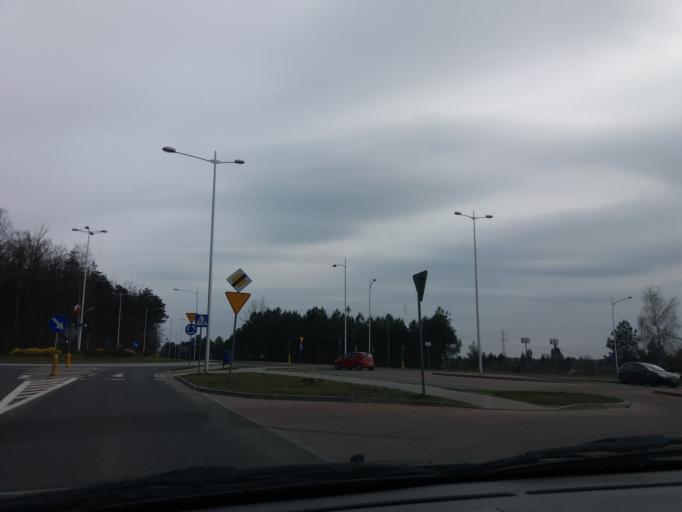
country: PL
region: Masovian Voivodeship
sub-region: Powiat mlawski
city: Mlawa
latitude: 53.1294
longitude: 20.3776
